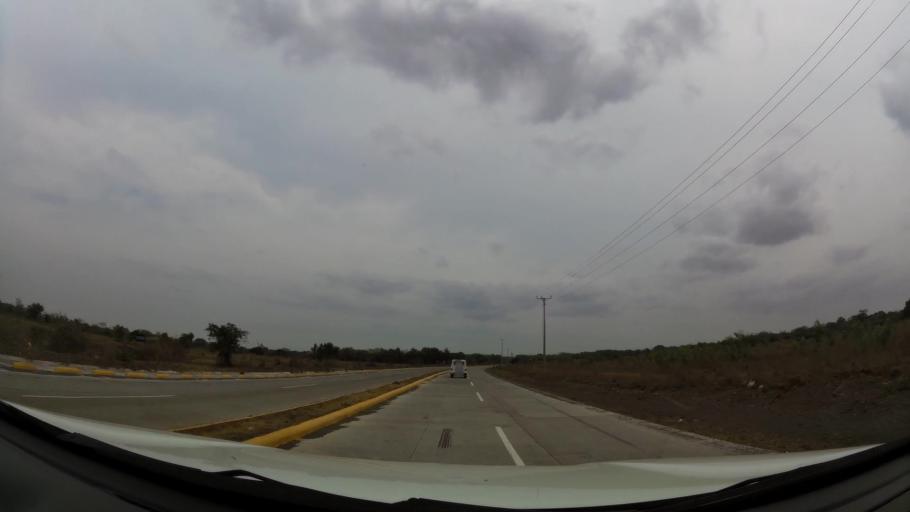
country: NI
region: Managua
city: Managua
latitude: 12.1135
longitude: -86.1728
